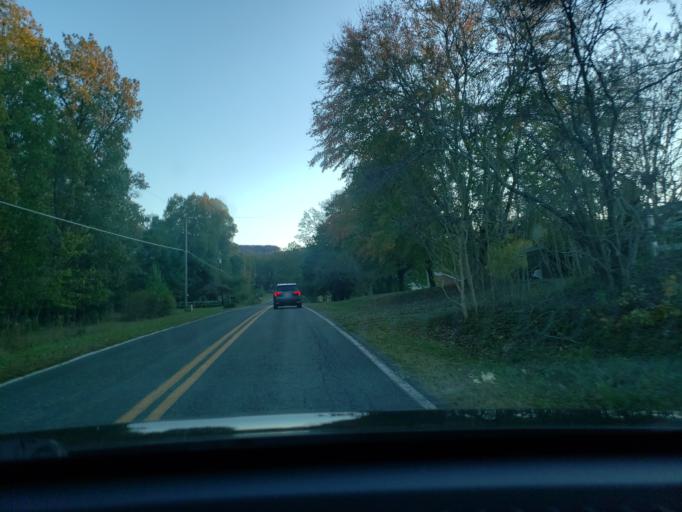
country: US
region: North Carolina
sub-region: Stokes County
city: Danbury
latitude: 36.4188
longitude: -80.2446
